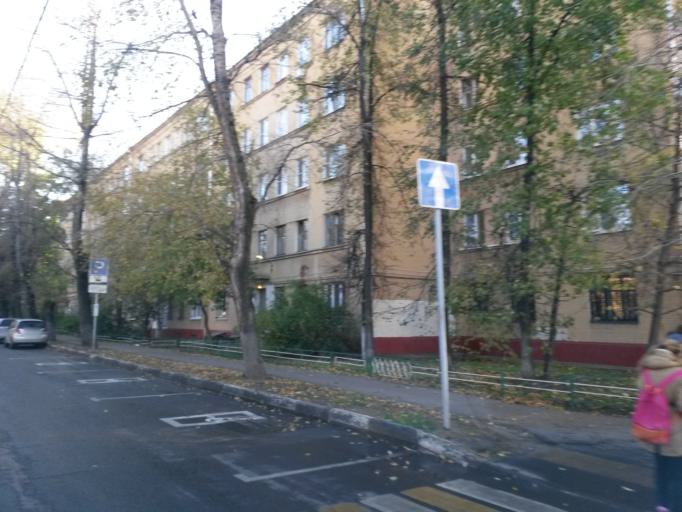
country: RU
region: Moscow
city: Zamoskvorech'ye
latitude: 55.7167
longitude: 37.6137
